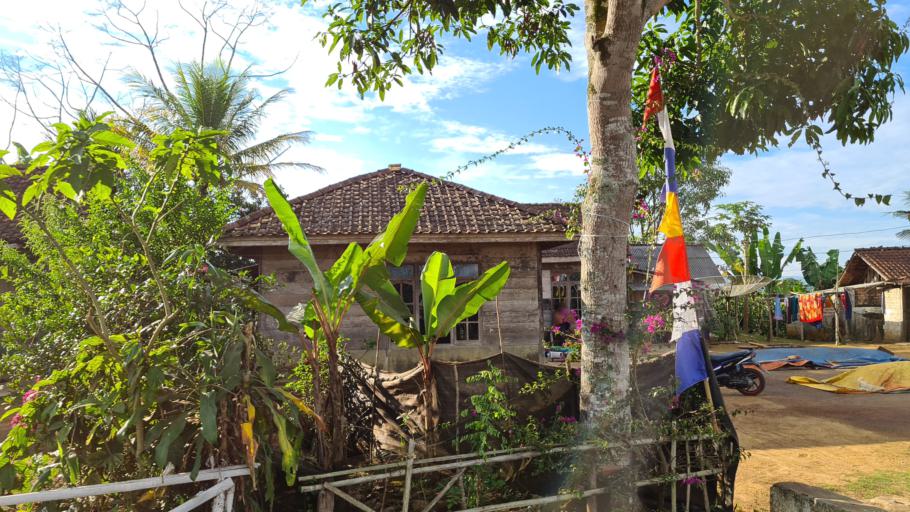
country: ID
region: Lampung
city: Kenali
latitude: -5.0936
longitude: 104.3992
